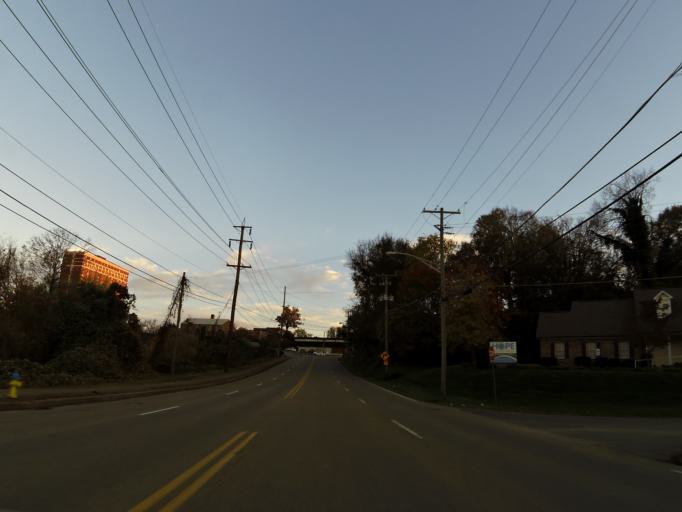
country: US
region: Tennessee
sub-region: Knox County
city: Knoxville
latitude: 35.9547
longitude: -83.9483
